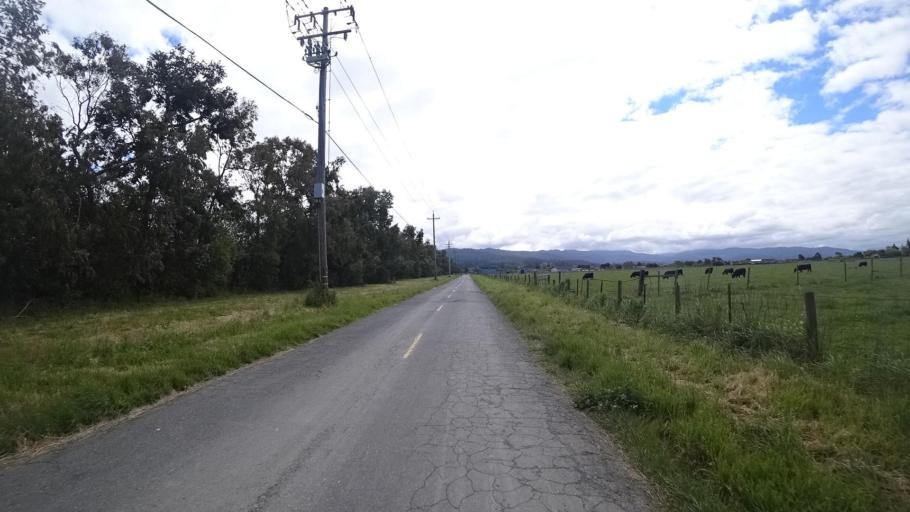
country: US
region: California
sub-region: Humboldt County
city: Arcata
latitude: 40.8826
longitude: -124.1063
